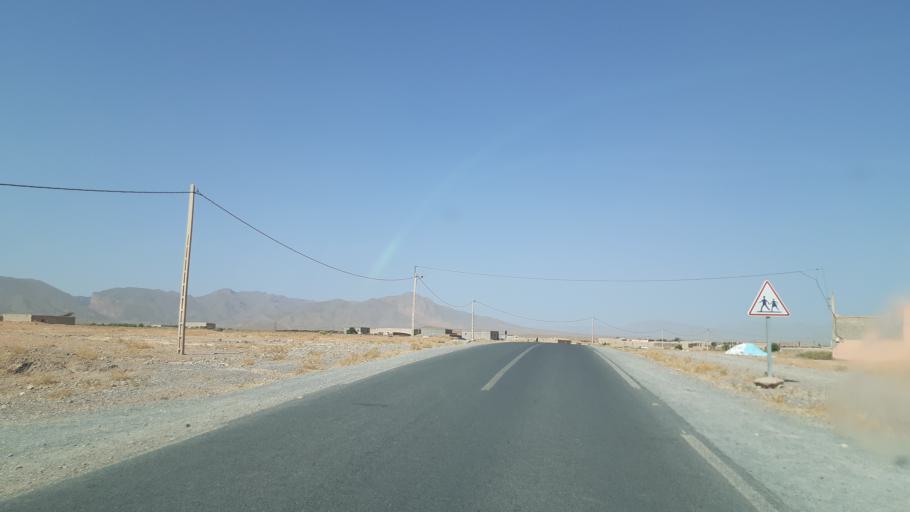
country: MA
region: Meknes-Tafilalet
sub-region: Errachidia
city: Amouguer
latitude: 32.2376
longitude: -4.6117
